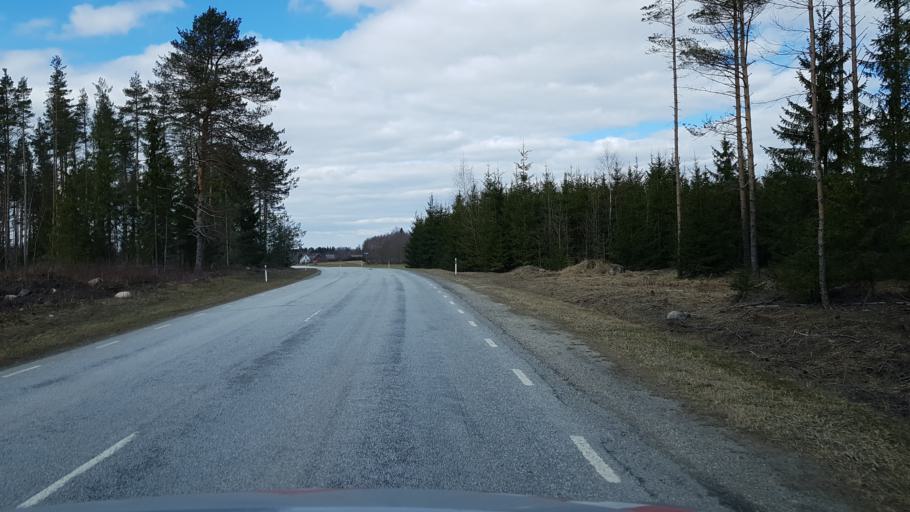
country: EE
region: Laeaene-Virumaa
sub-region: Rakke vald
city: Rakke
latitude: 58.9793
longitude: 26.2669
